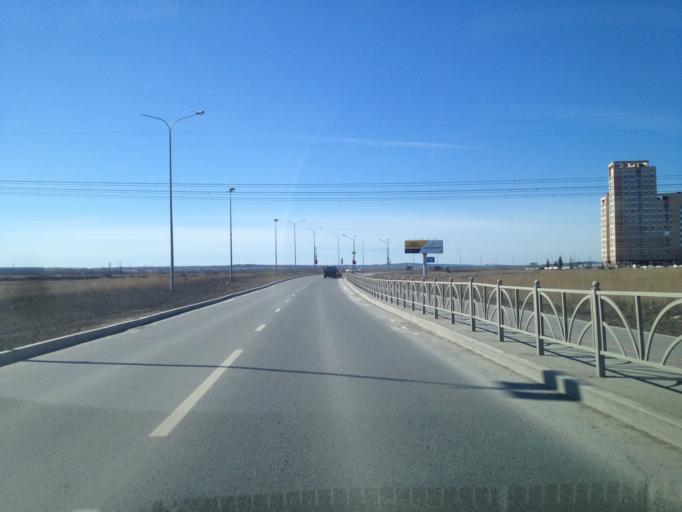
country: RU
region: Sverdlovsk
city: Sovkhoznyy
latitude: 56.7480
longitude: 60.5758
